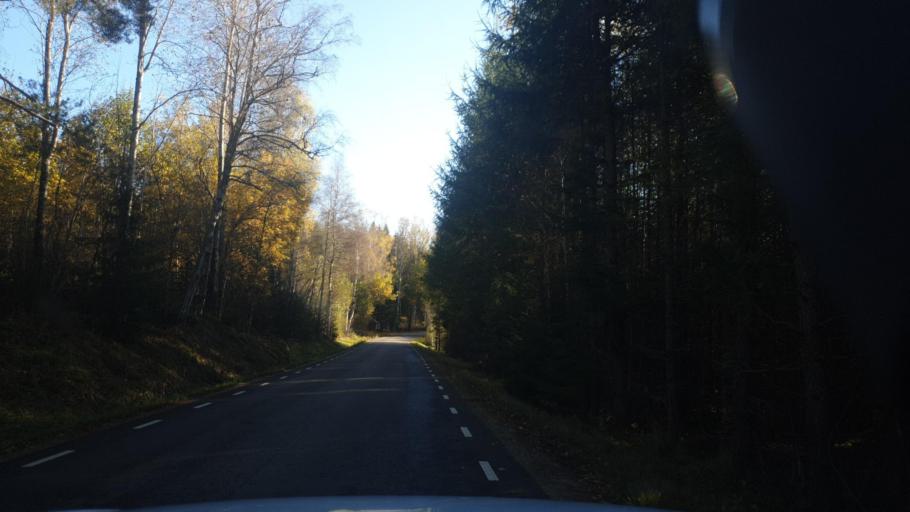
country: SE
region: Vaermland
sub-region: Arvika Kommun
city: Arvika
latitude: 59.6535
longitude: 12.8069
